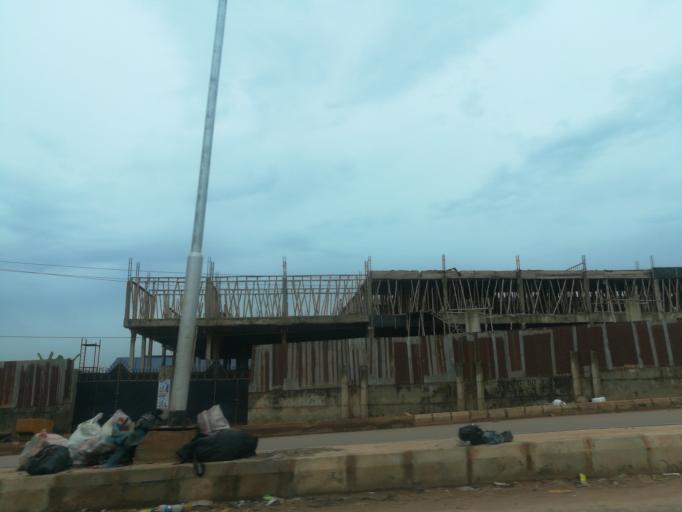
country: NG
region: Oyo
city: Ibadan
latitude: 7.3905
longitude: 3.9390
